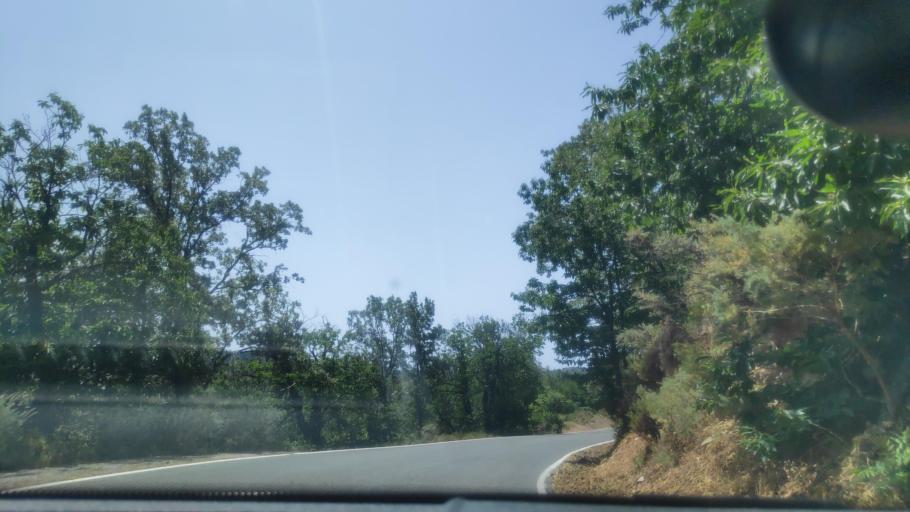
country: ES
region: Andalusia
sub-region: Provincia de Granada
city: Busquistar
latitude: 36.9630
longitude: -3.2802
